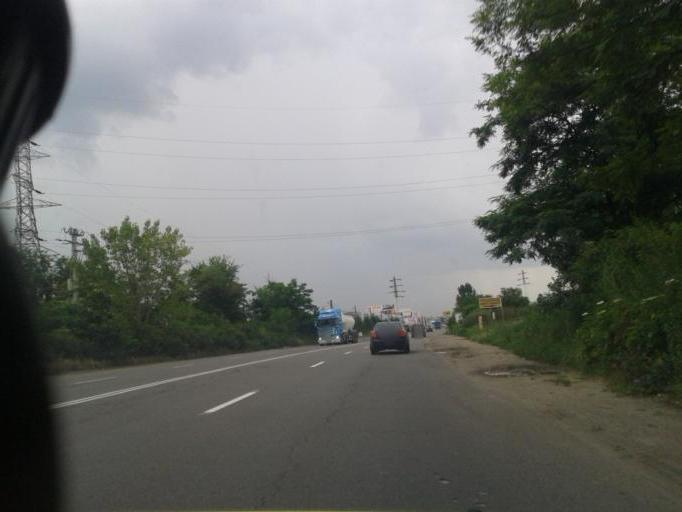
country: RO
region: Prahova
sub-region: Comuna Bucov
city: Bucov
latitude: 44.9624
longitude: 26.0599
